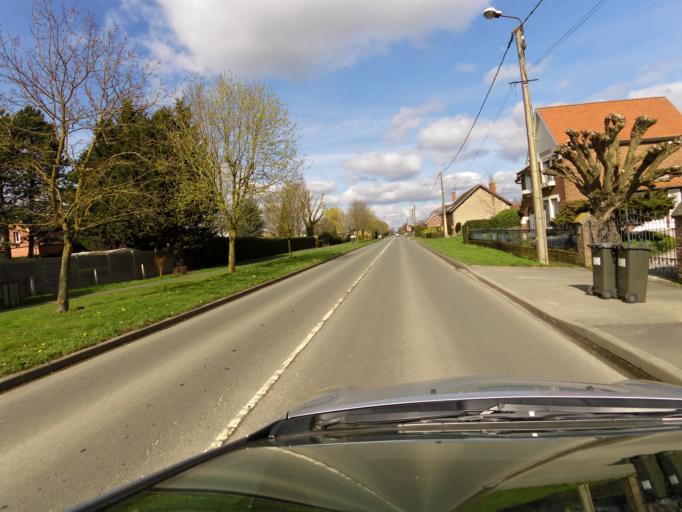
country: FR
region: Nord-Pas-de-Calais
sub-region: Departement du Nord
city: Aubers
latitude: 50.6096
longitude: 2.7980
